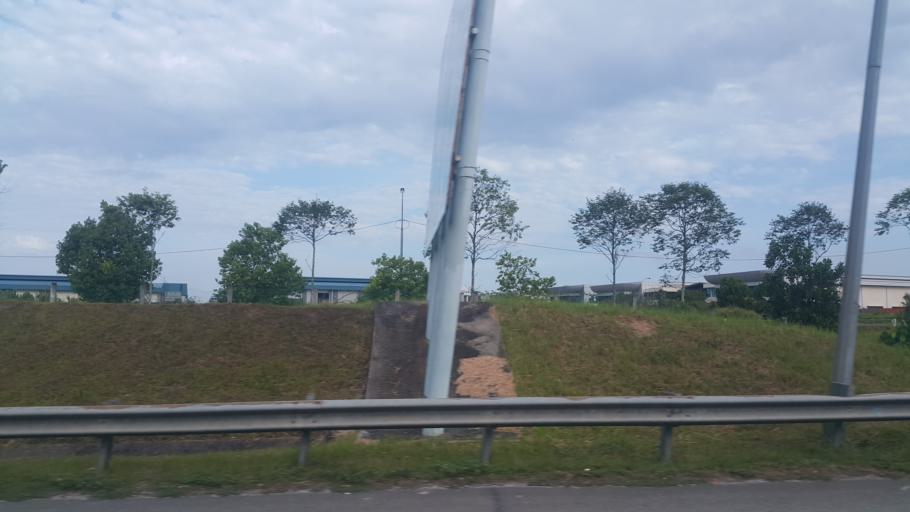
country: MY
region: Johor
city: Skudai
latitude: 1.4387
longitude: 103.6104
